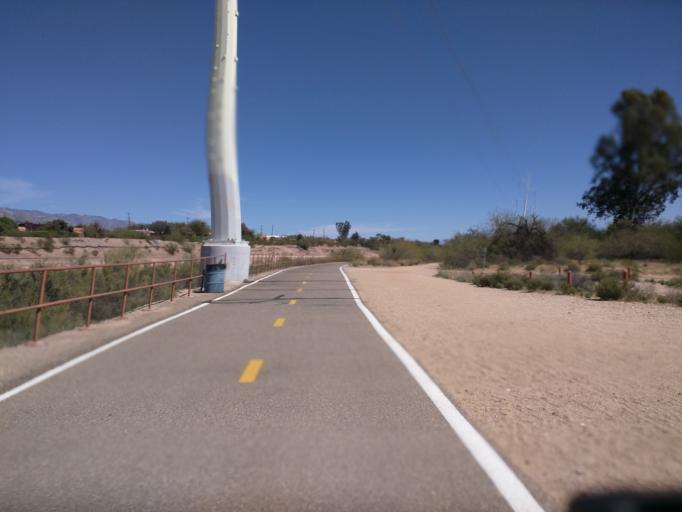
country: US
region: Arizona
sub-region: Pima County
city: Catalina Foothills
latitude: 32.2825
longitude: -110.9316
